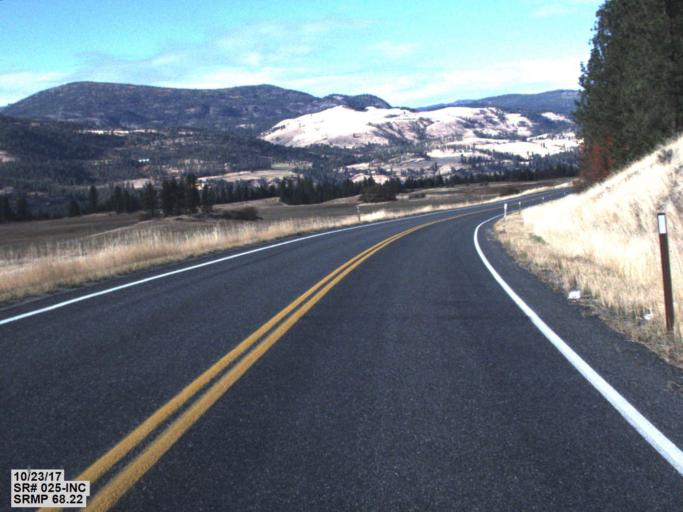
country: US
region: Washington
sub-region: Stevens County
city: Kettle Falls
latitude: 48.4544
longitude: -118.1780
